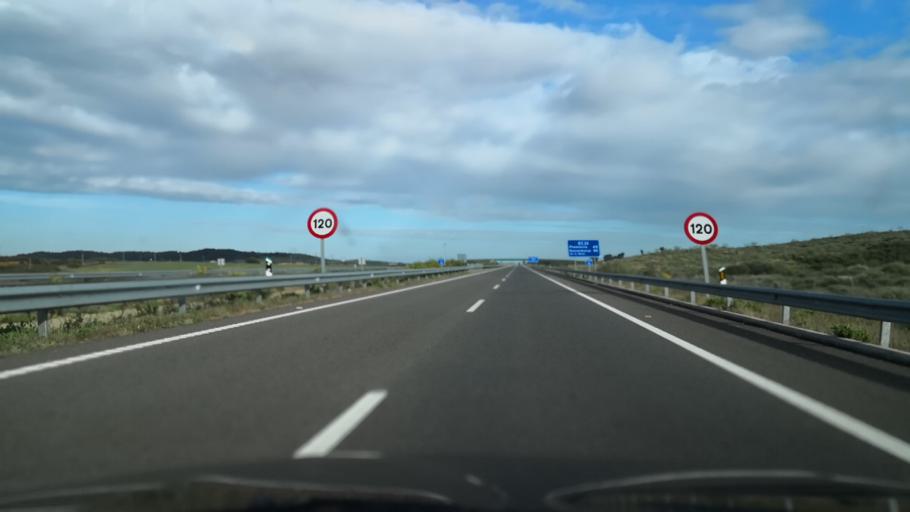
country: ES
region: Extremadura
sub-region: Provincia de Caceres
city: Casas de Don Gomez
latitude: 40.0223
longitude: -6.5979
